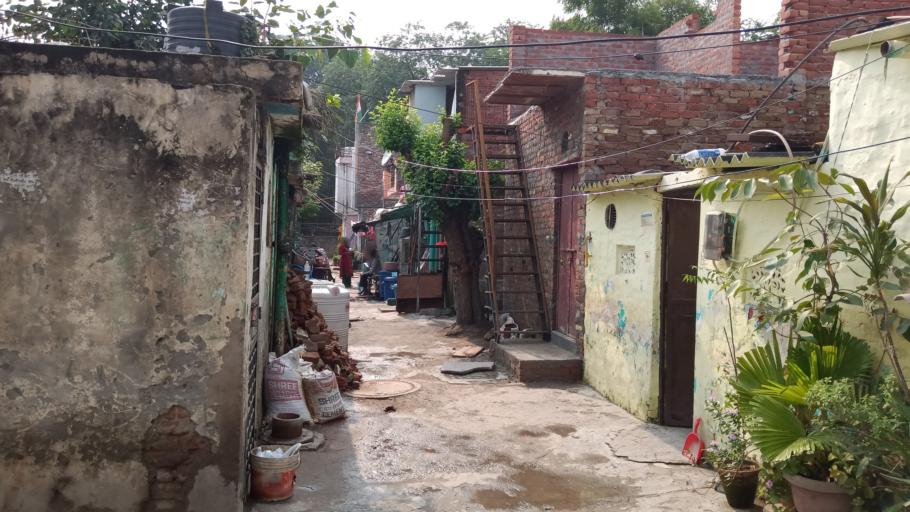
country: IN
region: NCT
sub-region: New Delhi
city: New Delhi
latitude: 28.5781
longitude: 77.2476
